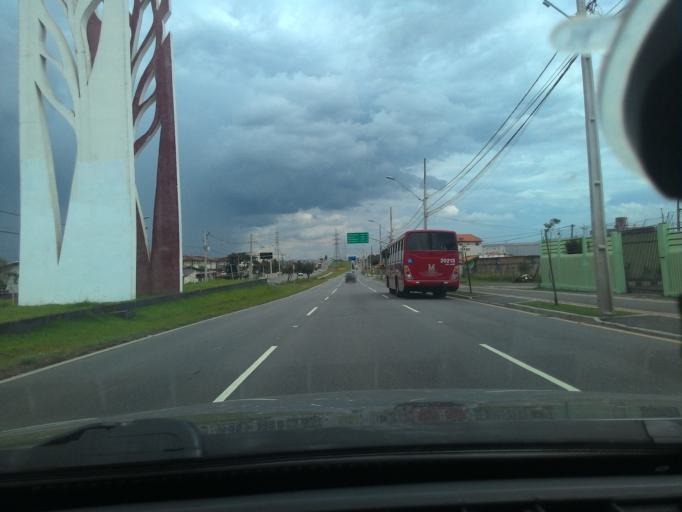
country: BR
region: Parana
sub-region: Sao Jose Dos Pinhais
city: Sao Jose dos Pinhais
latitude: -25.4961
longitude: -49.2120
